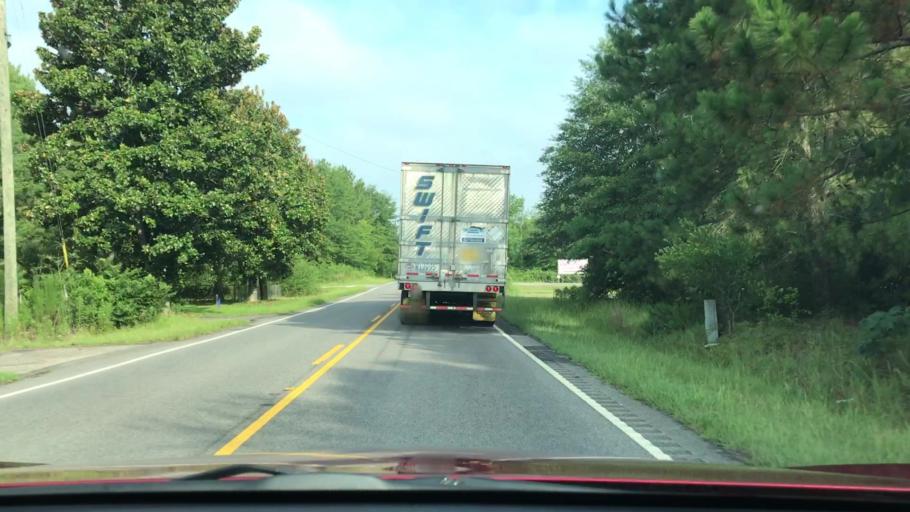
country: US
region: South Carolina
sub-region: Barnwell County
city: Williston
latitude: 33.6325
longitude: -81.3112
